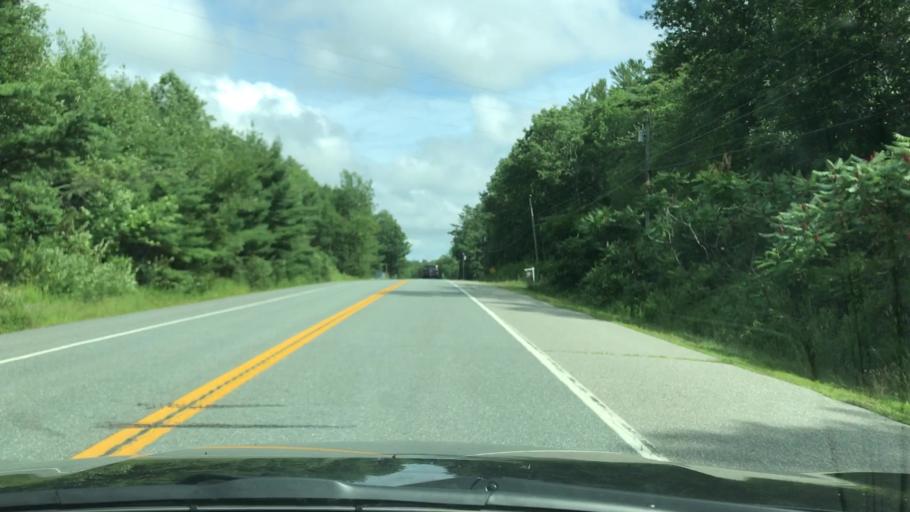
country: US
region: Maine
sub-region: Hancock County
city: Orland
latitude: 44.5664
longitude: -68.6713
